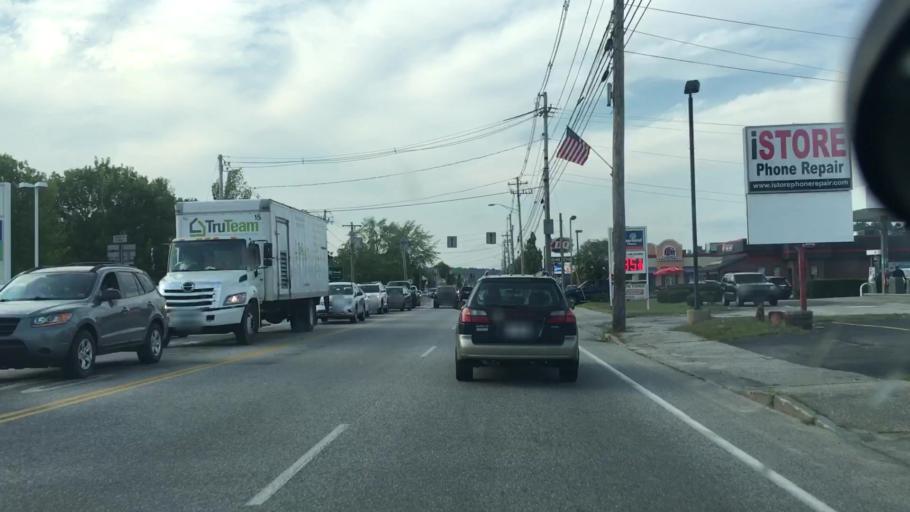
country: US
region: Maine
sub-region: Cumberland County
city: North Windham
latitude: 43.8344
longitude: -70.4384
